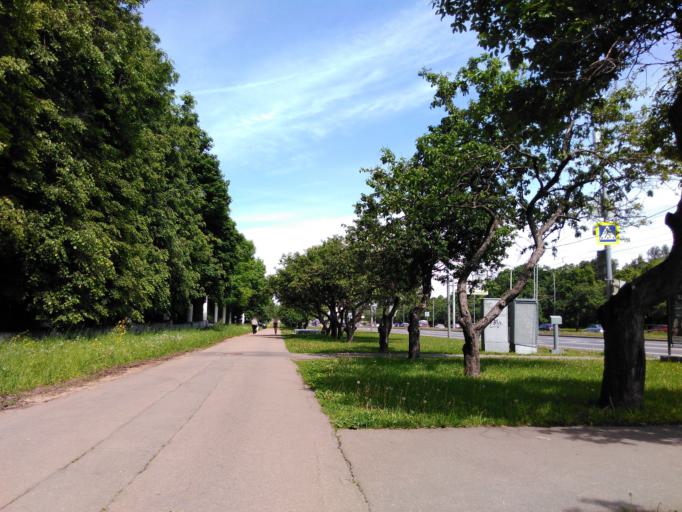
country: RU
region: Moskovskaya
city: Semenovskoye
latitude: 55.6976
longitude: 37.5413
